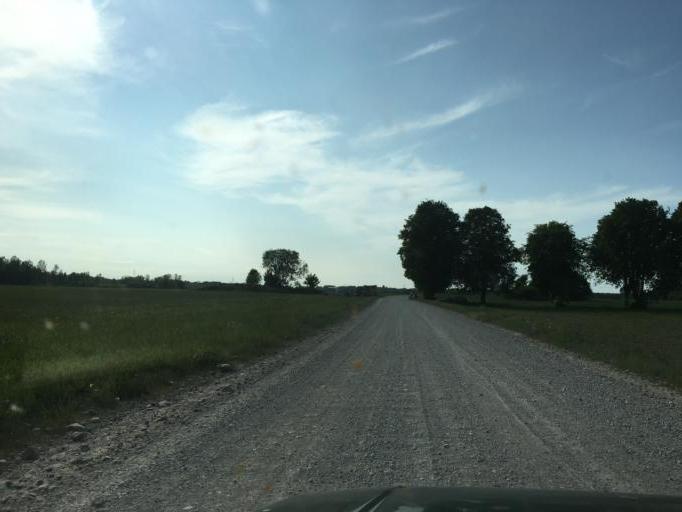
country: LV
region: Dundaga
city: Dundaga
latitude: 57.6215
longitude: 22.4130
